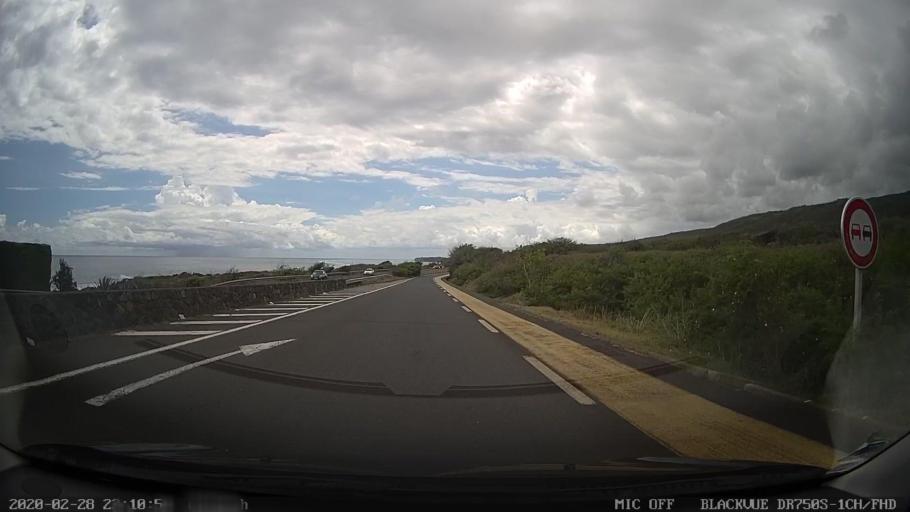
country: RE
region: Reunion
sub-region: Reunion
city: Trois-Bassins
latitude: -21.1152
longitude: 55.2574
